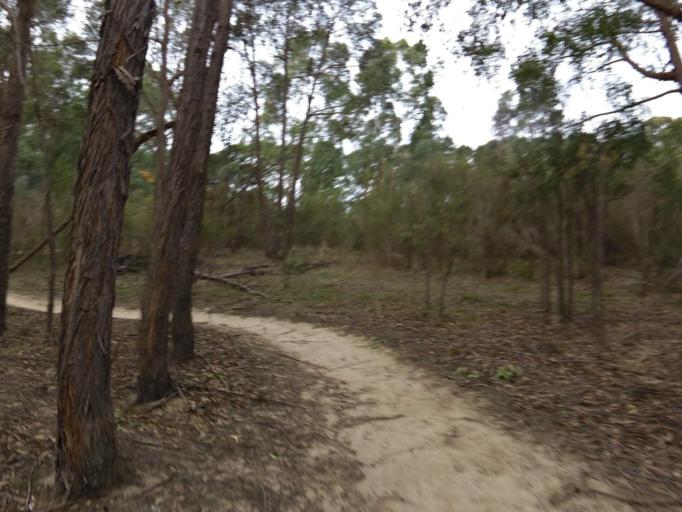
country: AU
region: Victoria
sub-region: Nillumbik
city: Eltham
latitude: -37.7452
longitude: 145.1438
